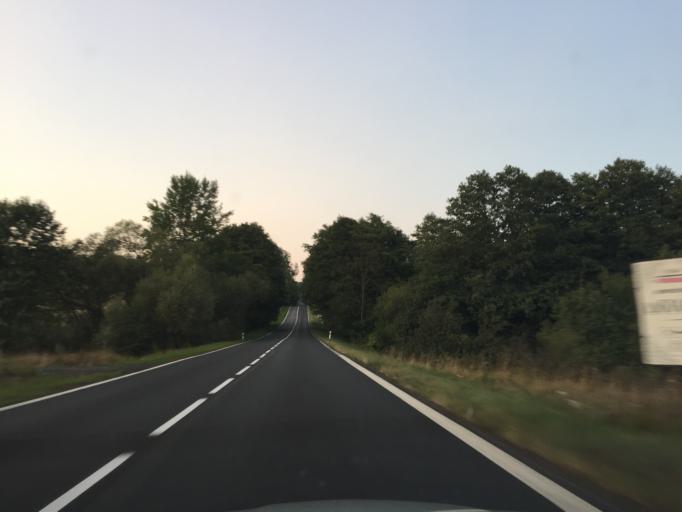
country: CZ
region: Ustecky
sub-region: Okres Decin
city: Chribska
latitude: 50.8652
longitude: 14.4915
